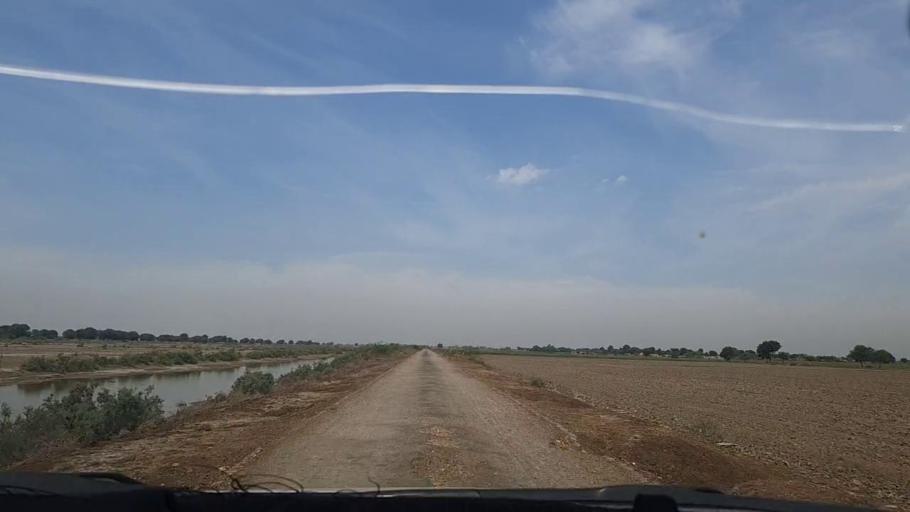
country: PK
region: Sindh
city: Pithoro
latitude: 25.4637
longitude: 69.4700
